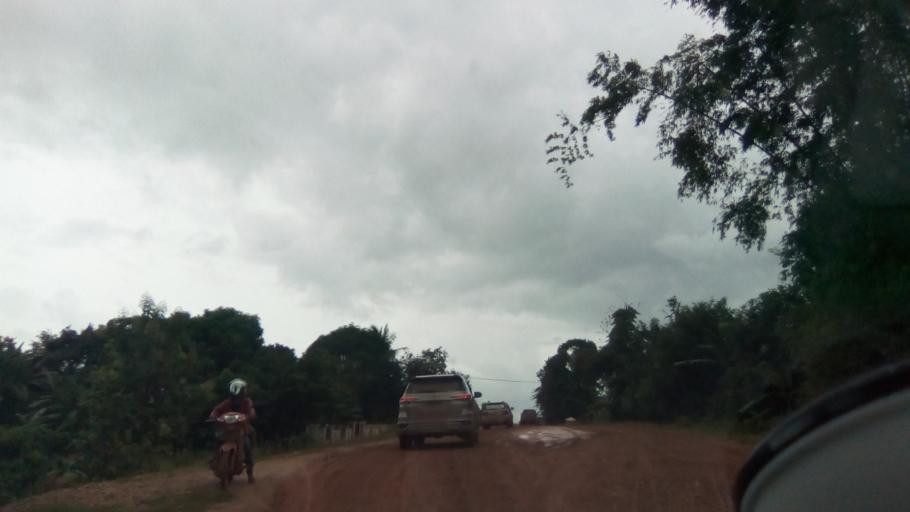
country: LA
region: Attapu
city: Attapu
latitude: 14.7428
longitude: 106.6929
